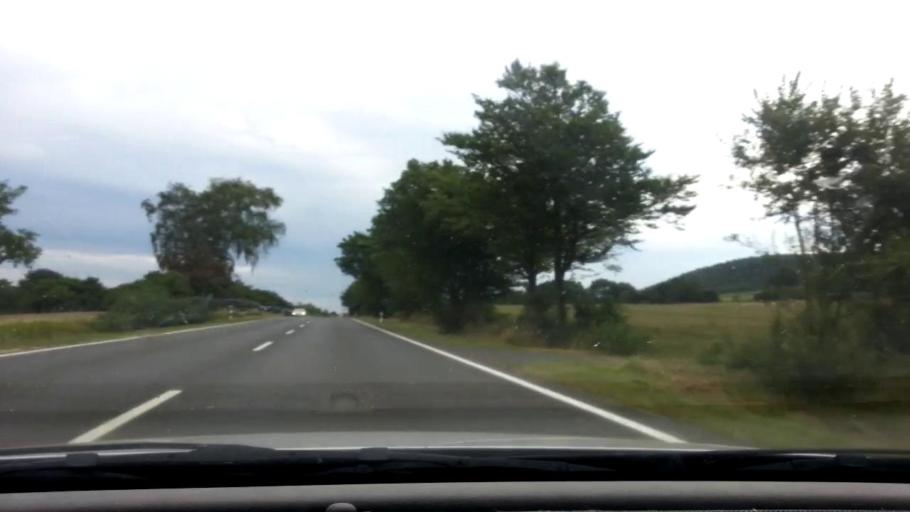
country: DE
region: Bavaria
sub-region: Upper Palatinate
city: Kastl
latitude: 49.8615
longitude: 11.9576
